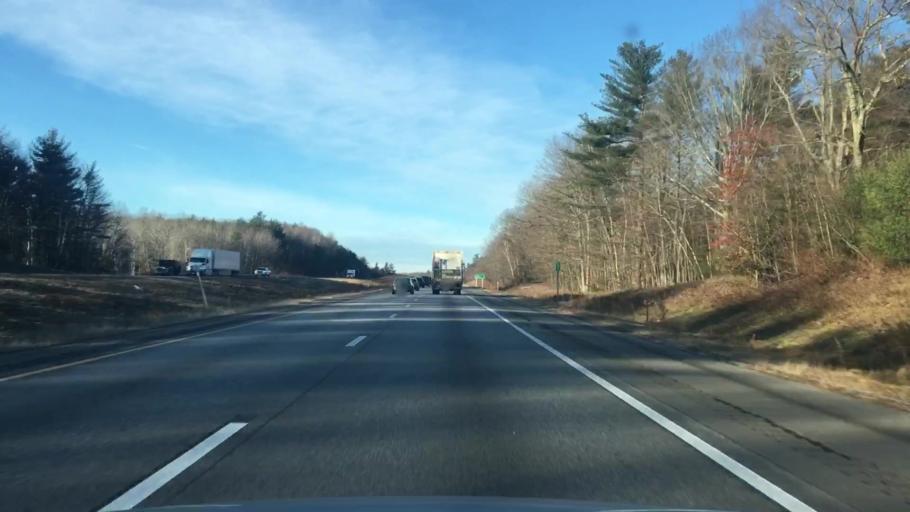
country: US
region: New Hampshire
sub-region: Rockingham County
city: Raymond
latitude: 43.0231
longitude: -71.2120
